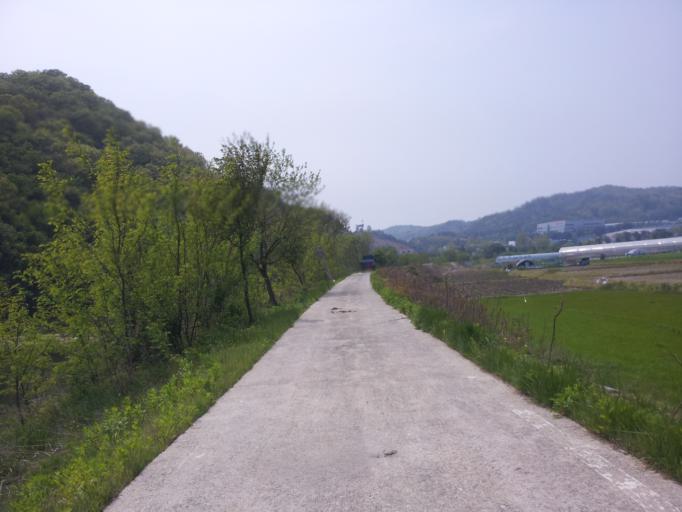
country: KR
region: Daejeon
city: Daejeon
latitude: 36.2571
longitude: 127.2878
